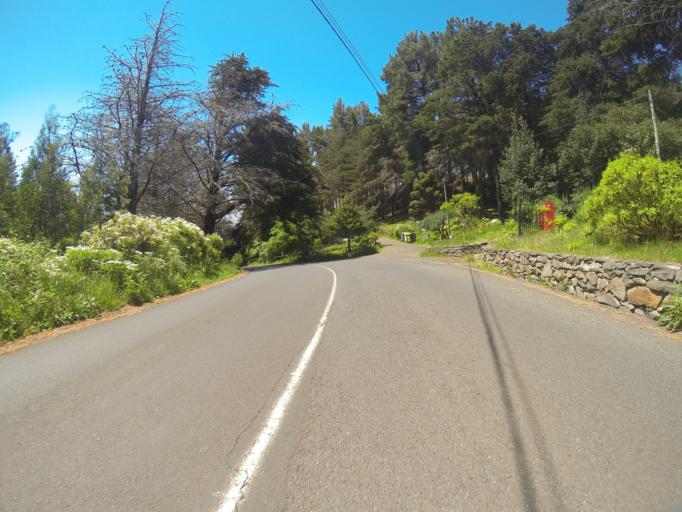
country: PT
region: Madeira
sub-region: Funchal
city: Nossa Senhora do Monte
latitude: 32.6970
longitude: -16.9040
